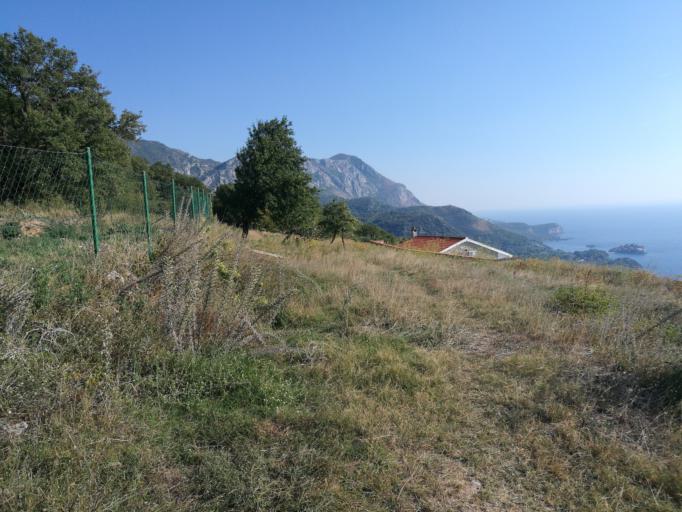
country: ME
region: Budva
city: Budva
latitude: 42.2825
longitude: 18.8921
